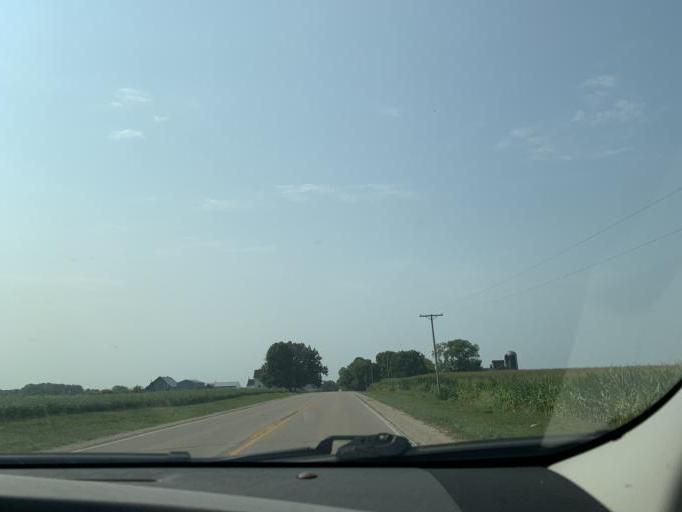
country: US
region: Illinois
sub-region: Whiteside County
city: Sterling
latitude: 41.8132
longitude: -89.7421
